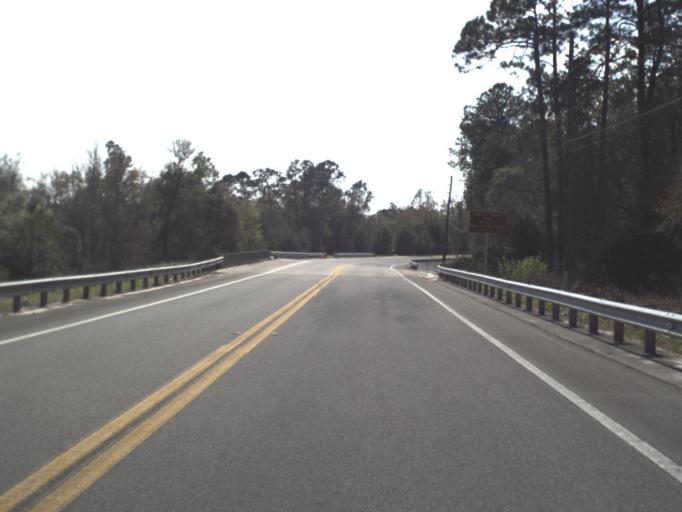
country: US
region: Florida
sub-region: Wakulla County
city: Crawfordville
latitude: 30.0694
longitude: -84.4508
